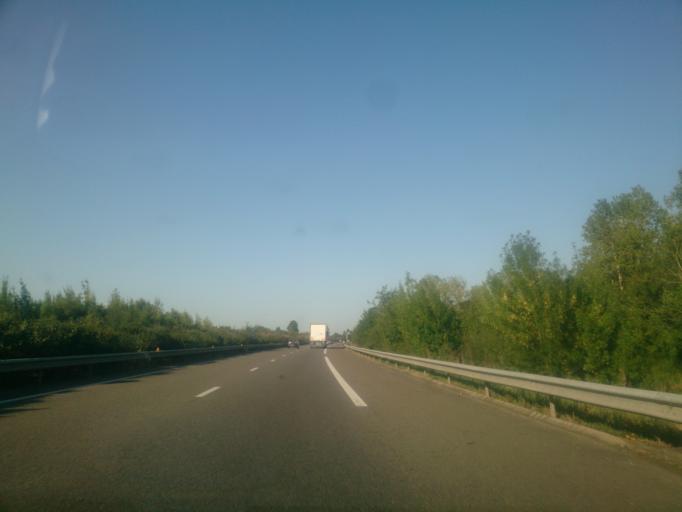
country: FR
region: Midi-Pyrenees
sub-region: Departement du Tarn-et-Garonne
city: Realville
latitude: 44.1285
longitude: 1.4818
